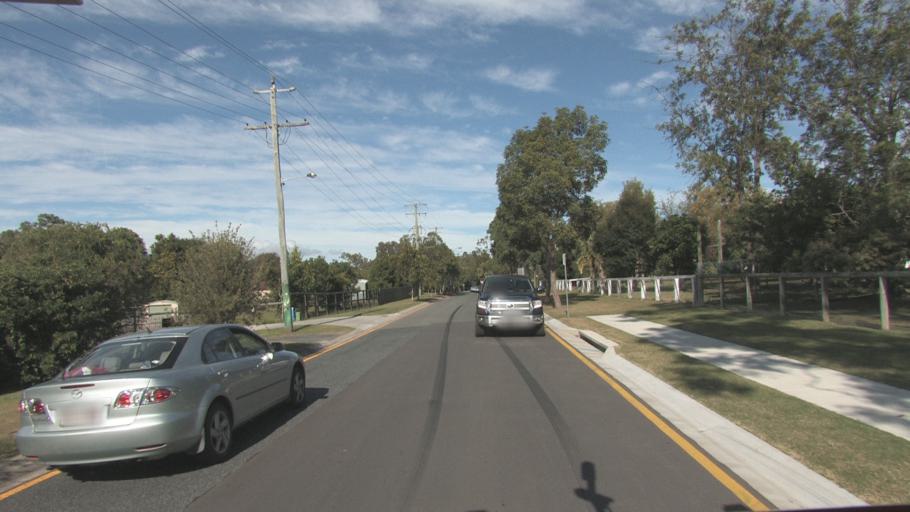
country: AU
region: Queensland
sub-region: Brisbane
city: Forest Lake
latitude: -27.6572
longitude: 152.9948
